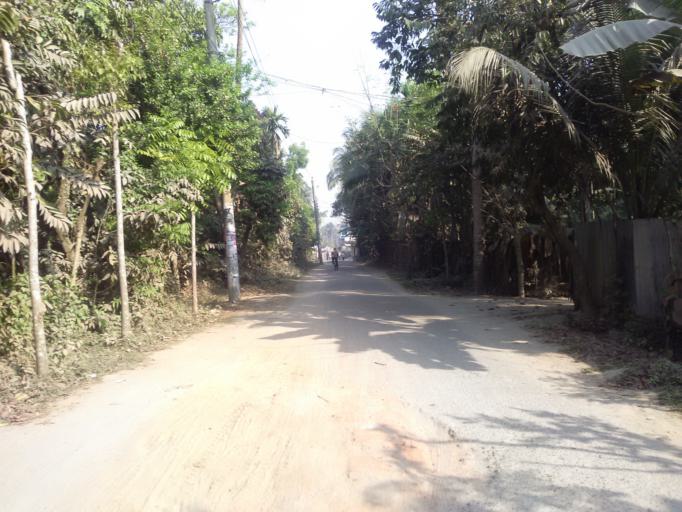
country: BD
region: Khulna
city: Khulna
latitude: 22.8973
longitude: 89.5227
